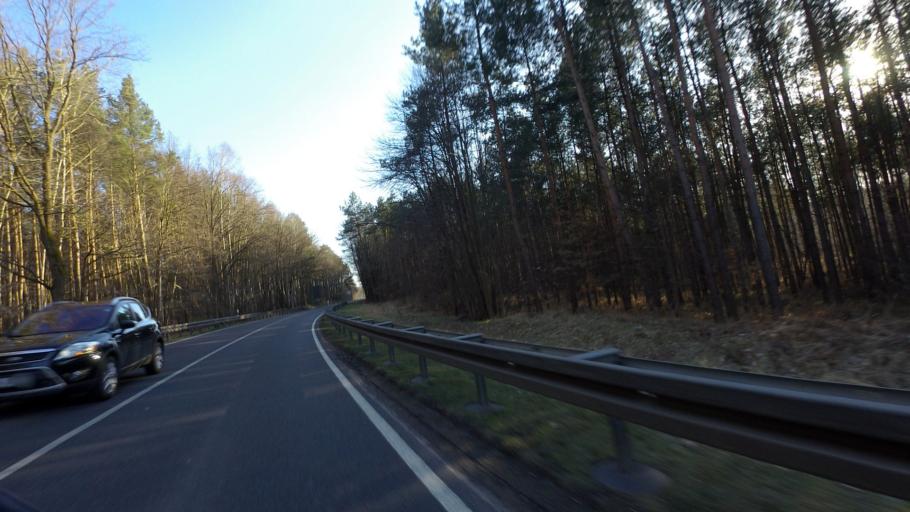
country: DE
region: Brandenburg
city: Althuttendorf
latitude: 52.9356
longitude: 13.7937
